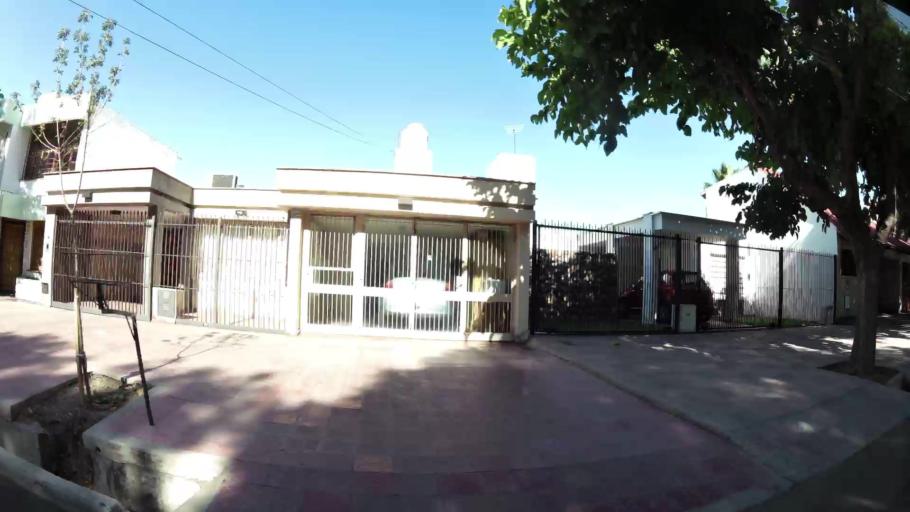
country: AR
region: Mendoza
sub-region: Departamento de Godoy Cruz
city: Godoy Cruz
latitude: -32.9246
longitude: -68.8322
